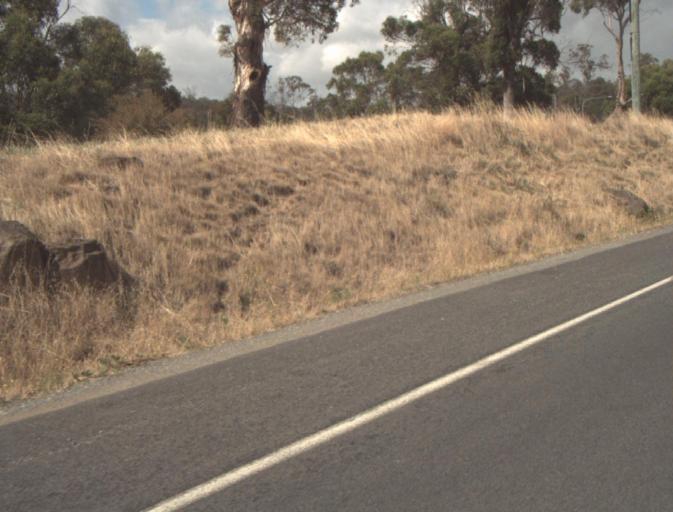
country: AU
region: Tasmania
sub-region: Launceston
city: Summerhill
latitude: -41.4831
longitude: 147.1530
